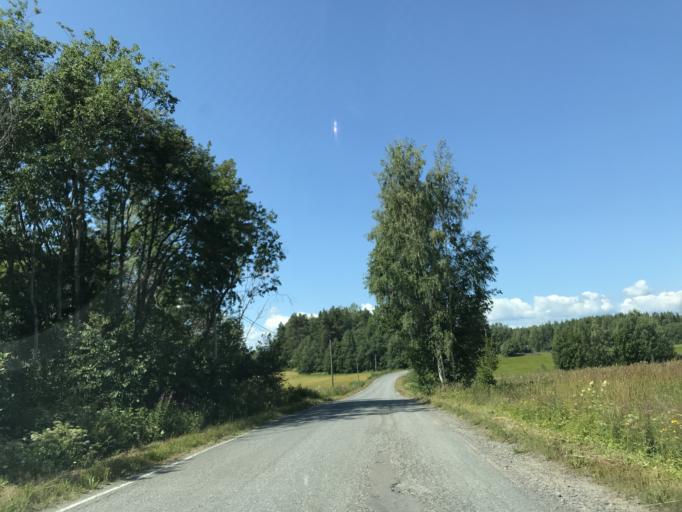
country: FI
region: Paijanne Tavastia
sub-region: Lahti
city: Asikkala
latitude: 61.1948
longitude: 25.6297
